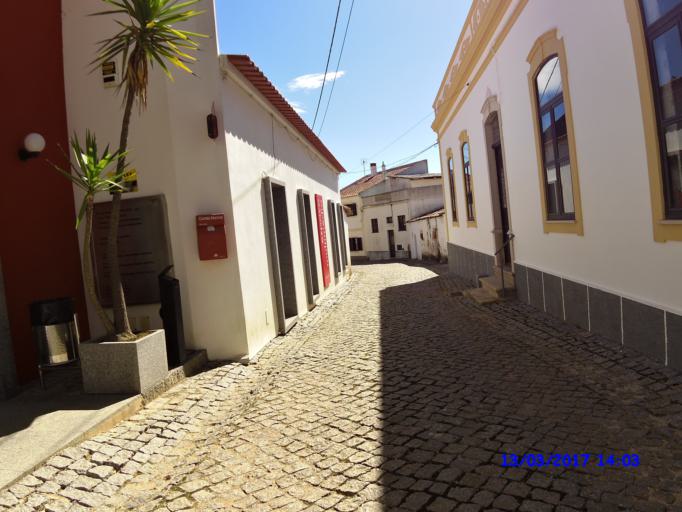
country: PT
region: Faro
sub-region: Monchique
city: Monchique
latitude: 37.3120
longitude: -8.6695
